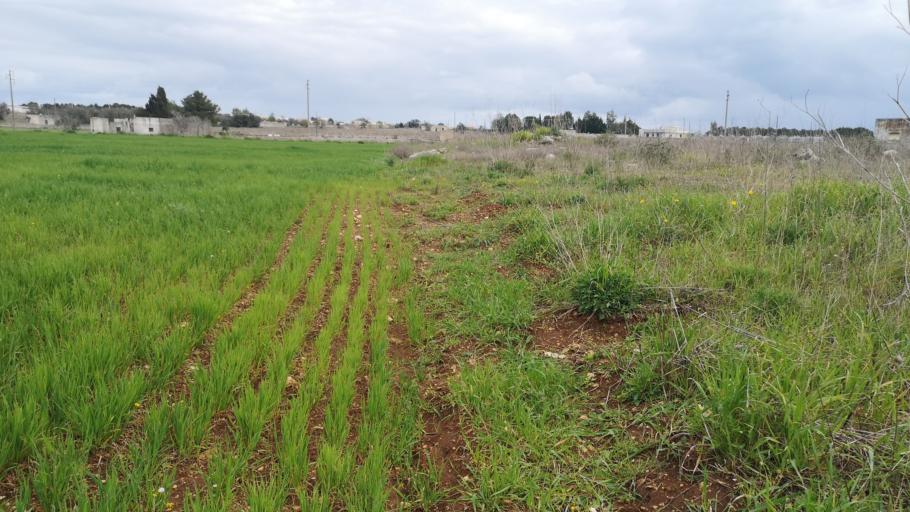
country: IT
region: Apulia
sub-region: Provincia di Lecce
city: Ortelle
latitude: 40.0288
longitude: 18.3798
